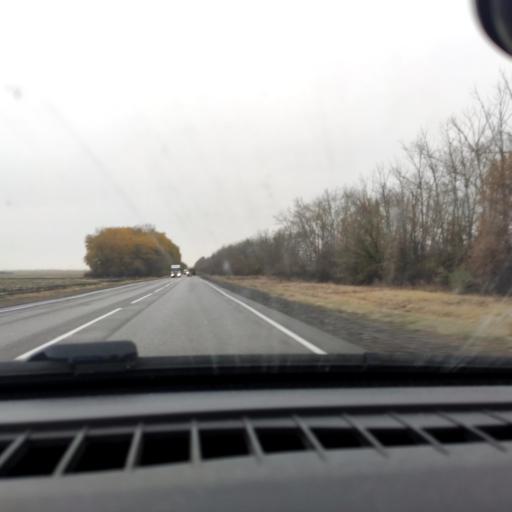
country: RU
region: Voronezj
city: Ostrogozhsk
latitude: 50.9541
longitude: 39.0395
